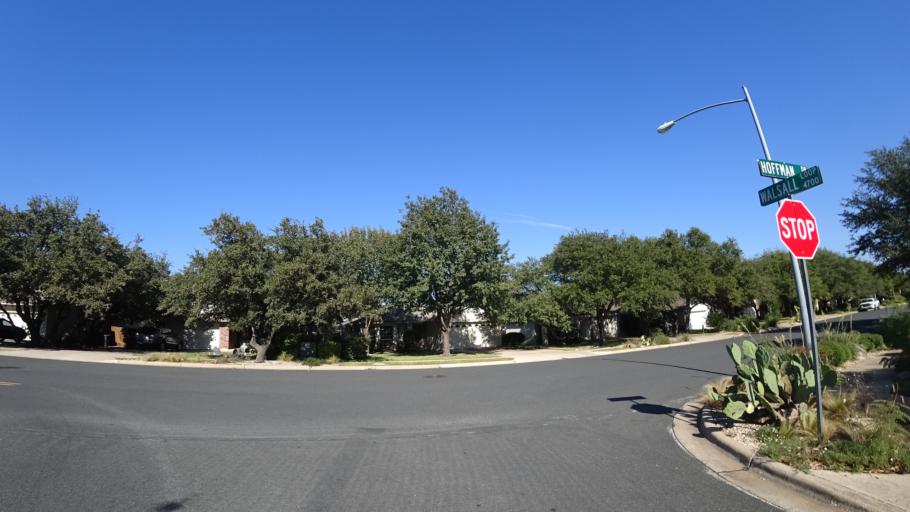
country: US
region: Texas
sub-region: Travis County
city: Shady Hollow
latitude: 30.1995
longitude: -97.8611
